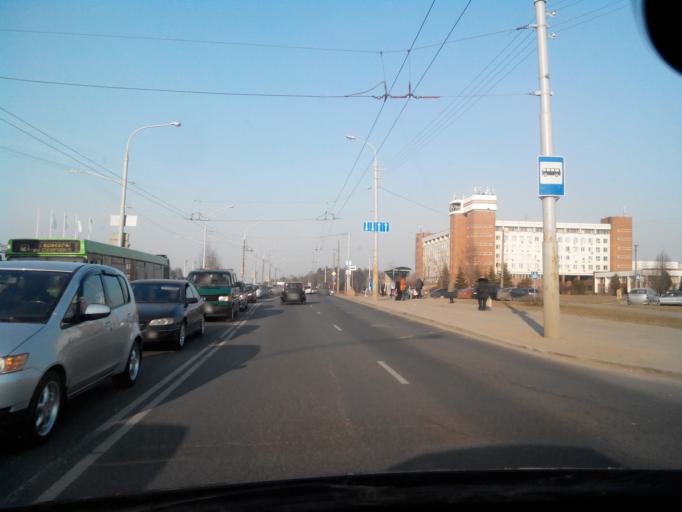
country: BY
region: Minsk
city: Novoye Medvezhino
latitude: 53.8851
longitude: 27.4482
